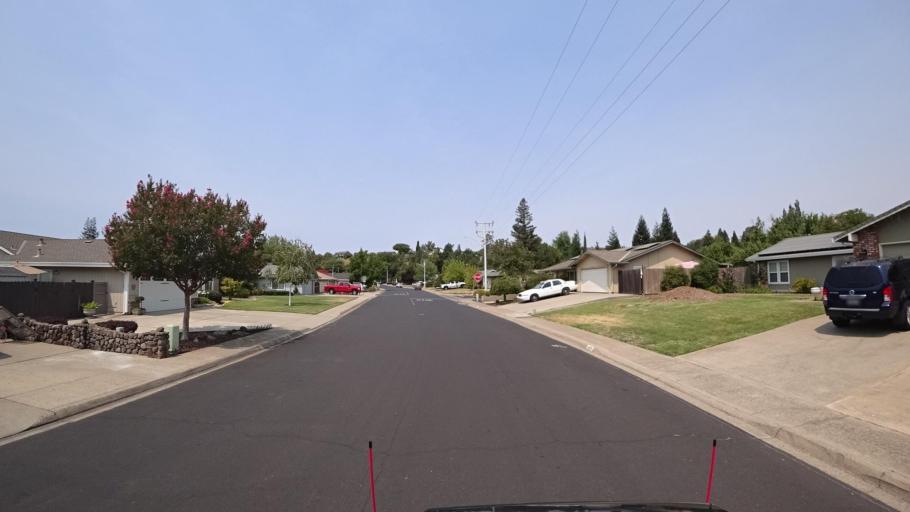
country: US
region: California
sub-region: Placer County
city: Rocklin
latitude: 38.8021
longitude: -121.2518
